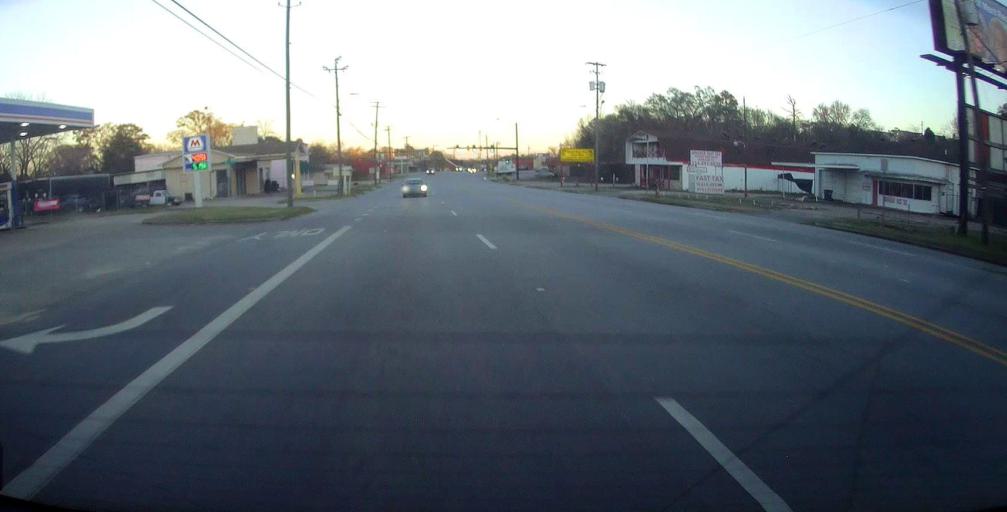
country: US
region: Alabama
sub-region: Russell County
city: Phenix City
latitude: 32.4748
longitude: -85.0232
